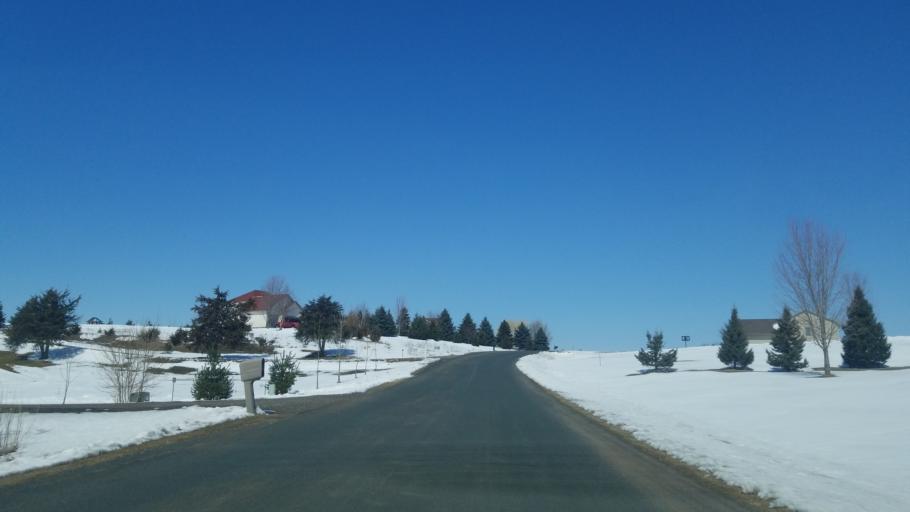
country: US
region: Wisconsin
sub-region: Saint Croix County
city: North Hudson
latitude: 44.9942
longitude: -92.6584
